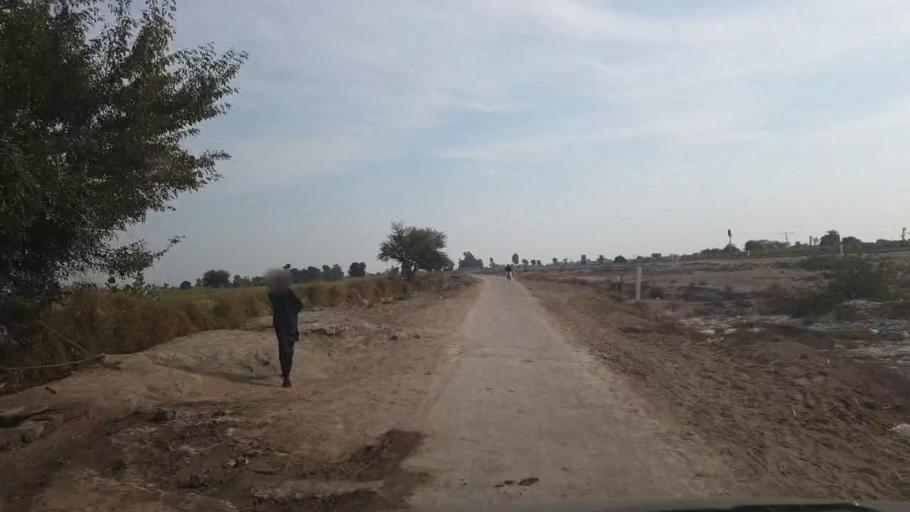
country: PK
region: Sindh
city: Nawabshah
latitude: 26.0920
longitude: 68.4828
